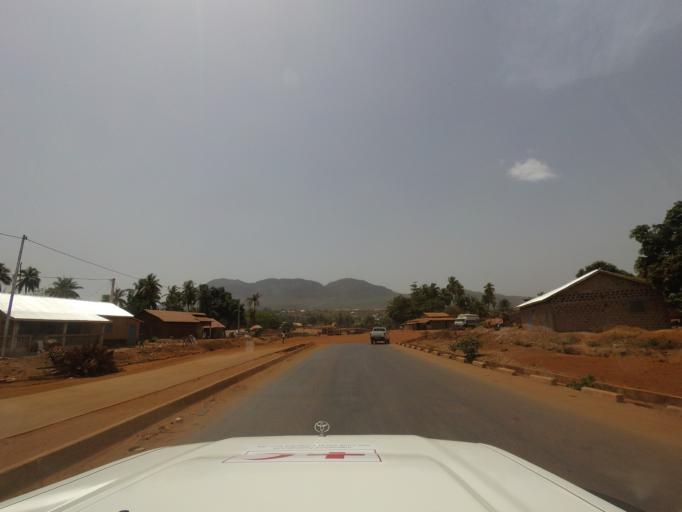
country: GN
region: Kindia
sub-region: Coyah
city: Coyah
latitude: 9.7258
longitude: -13.4163
